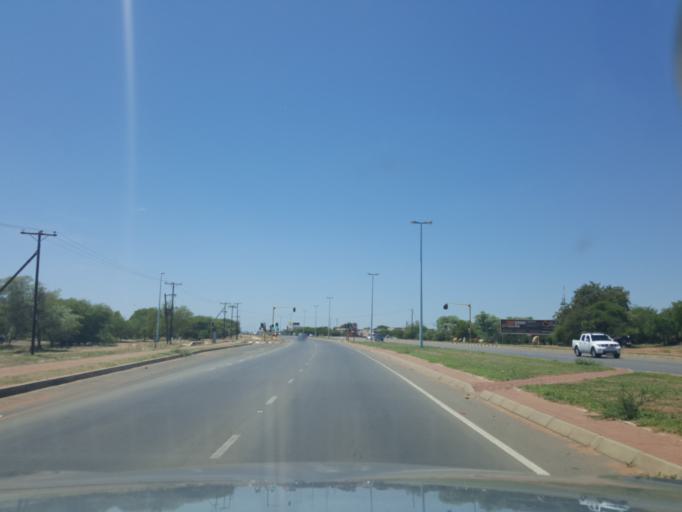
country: BW
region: Kweneng
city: Mogoditshane
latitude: -24.6015
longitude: 25.8548
